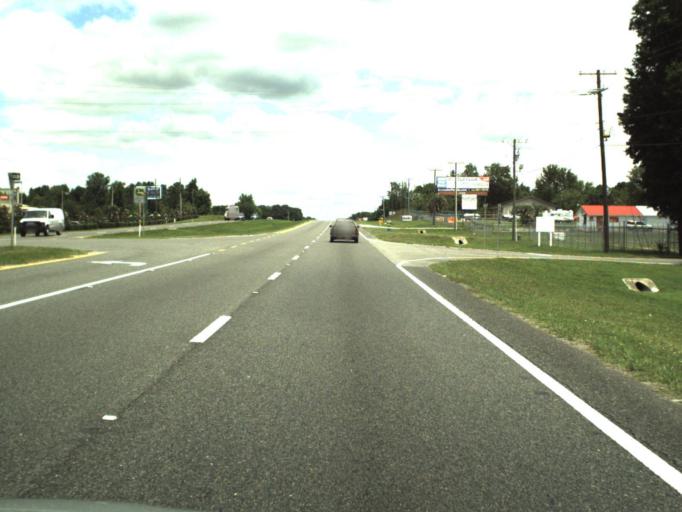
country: US
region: Florida
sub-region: Marion County
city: Ocala
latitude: 29.2518
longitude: -82.1520
